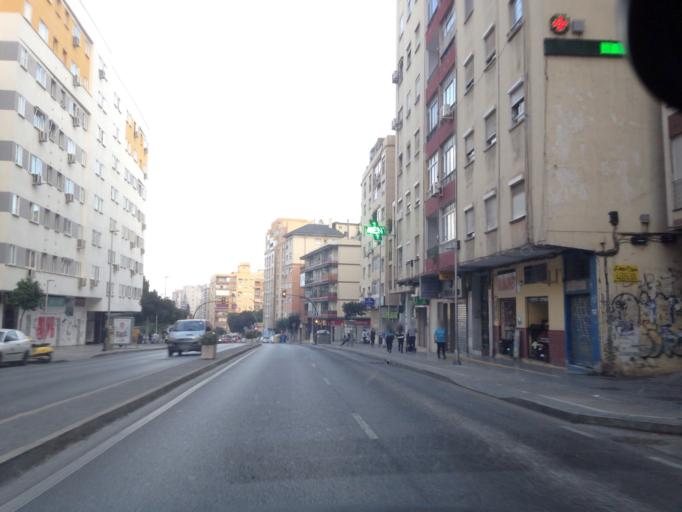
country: ES
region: Andalusia
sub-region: Provincia de Malaga
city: Malaga
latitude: 36.7217
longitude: -4.4446
